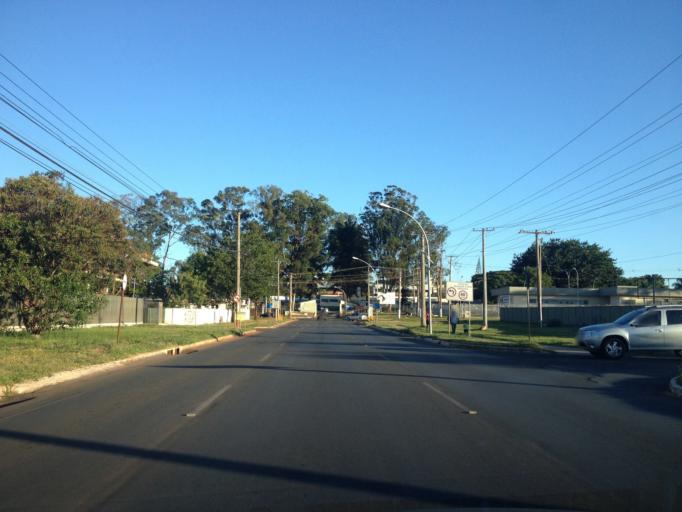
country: BR
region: Federal District
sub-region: Brasilia
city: Brasilia
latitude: -15.7569
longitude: -47.8977
